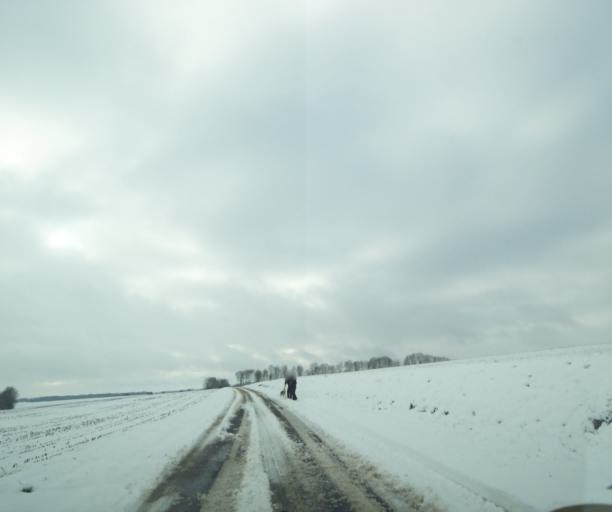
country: FR
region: Champagne-Ardenne
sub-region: Departement de la Haute-Marne
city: Montier-en-Der
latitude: 48.5064
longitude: 4.6873
